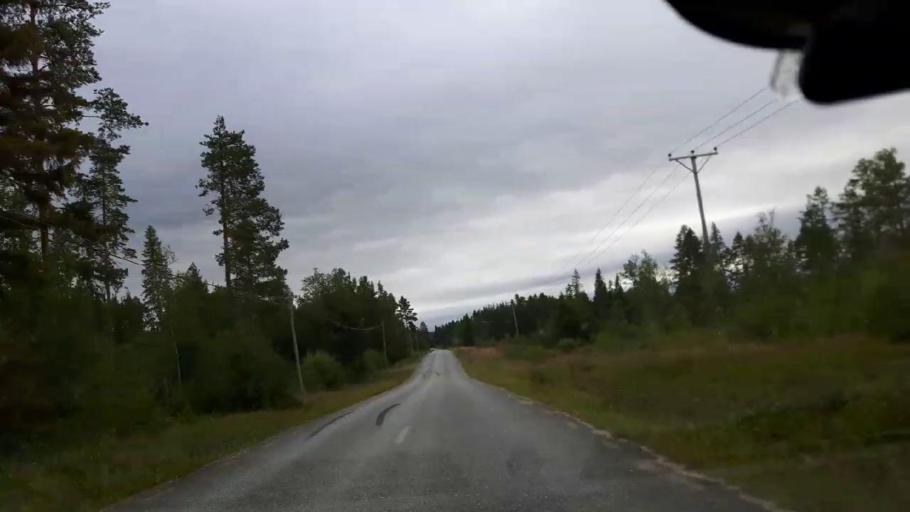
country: SE
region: Jaemtland
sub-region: Braecke Kommun
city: Braecke
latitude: 62.8838
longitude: 15.6188
